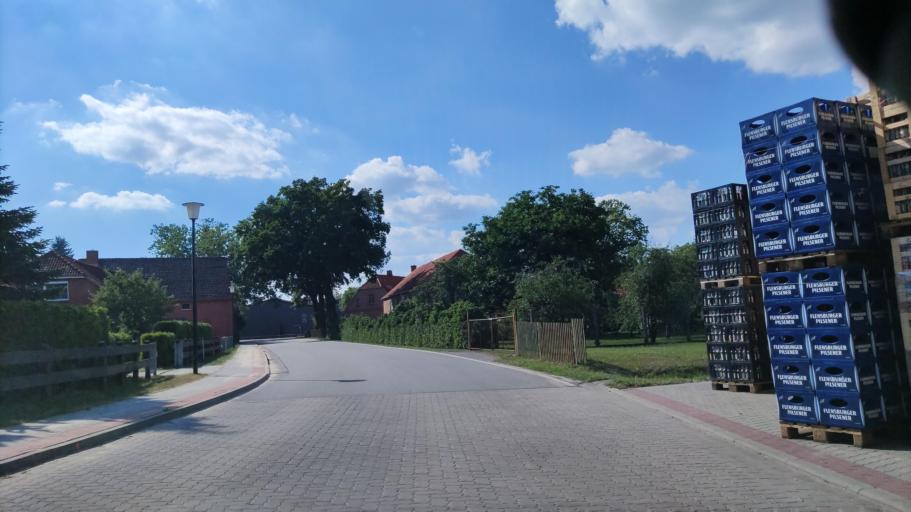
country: DE
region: Mecklenburg-Vorpommern
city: Lubtheen
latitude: 53.2349
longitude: 11.1389
